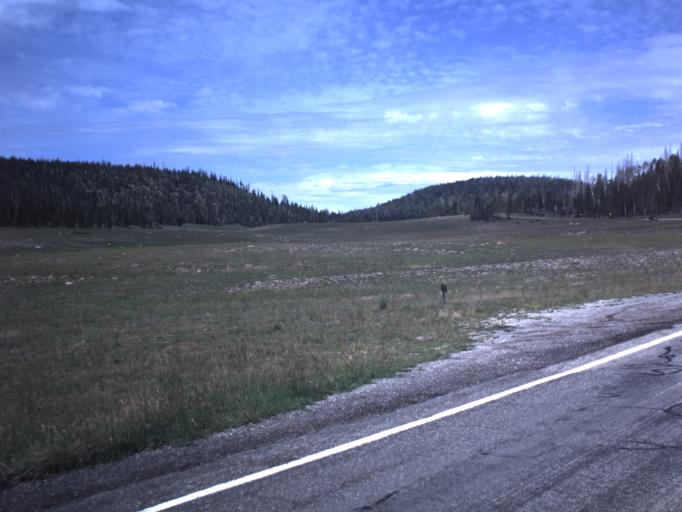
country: US
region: Utah
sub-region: Iron County
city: Cedar City
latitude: 37.5722
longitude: -112.8201
